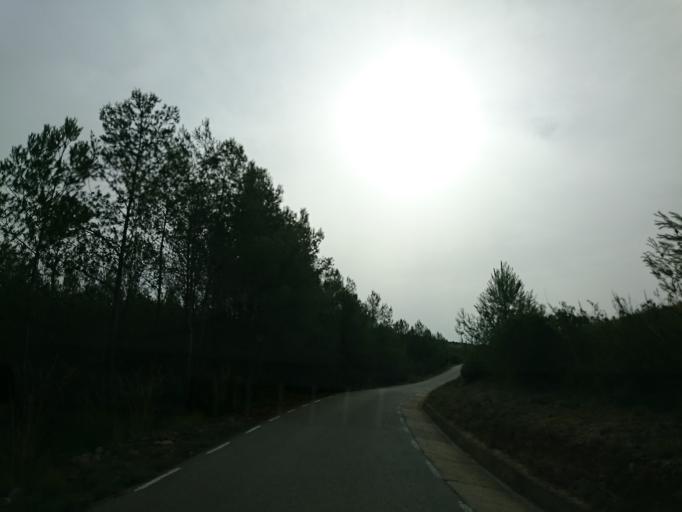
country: ES
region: Catalonia
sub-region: Provincia de Barcelona
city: Olivella
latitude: 41.3022
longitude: 1.8471
